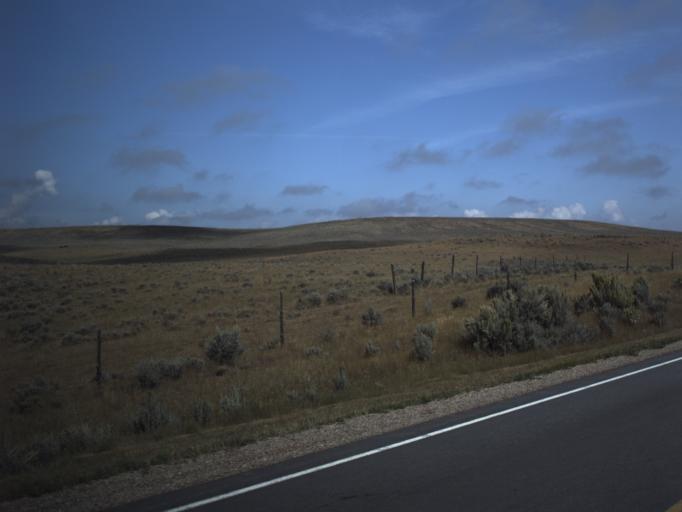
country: US
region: Utah
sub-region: Rich County
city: Randolph
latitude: 41.7569
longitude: -111.1375
